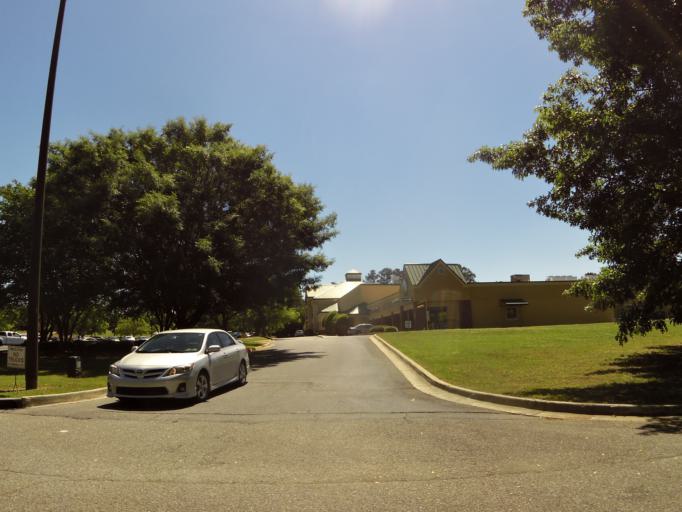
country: US
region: Georgia
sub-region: Columbia County
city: Martinez
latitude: 33.5086
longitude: -82.0324
